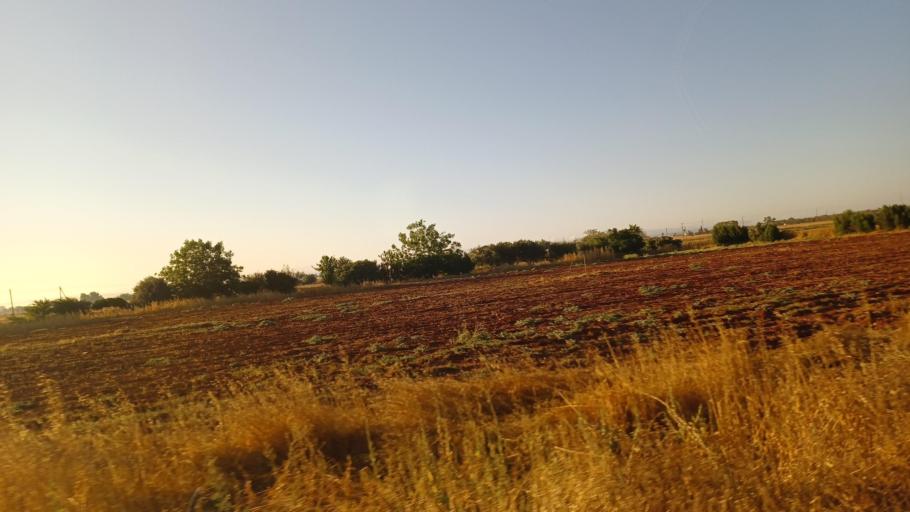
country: CY
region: Ammochostos
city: Avgorou
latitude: 35.0111
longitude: 33.8353
